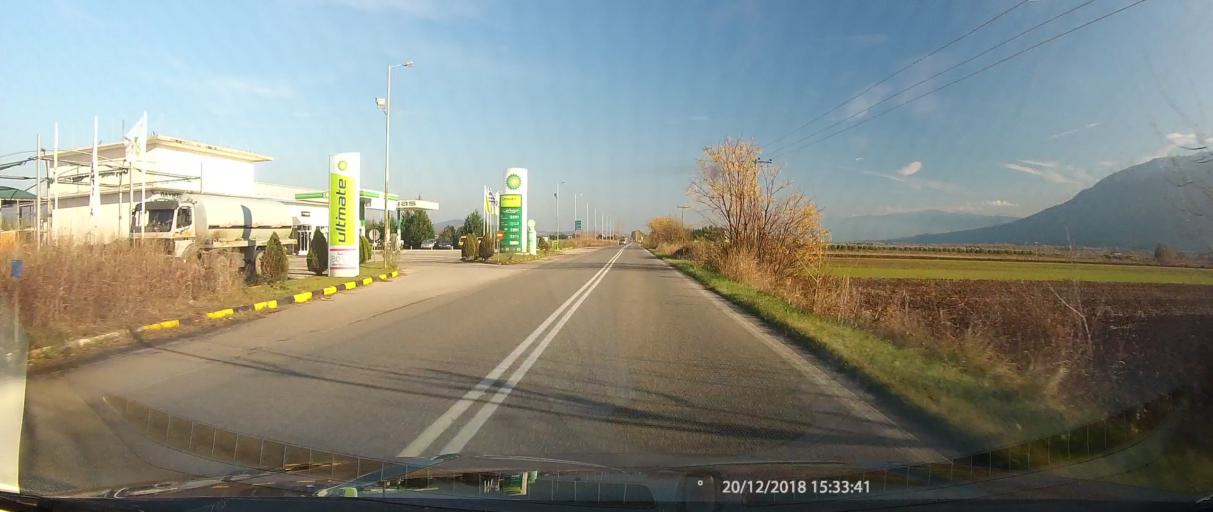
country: GR
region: Central Greece
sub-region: Nomos Fthiotidos
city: Lianokladhion
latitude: 38.9225
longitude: 22.2808
